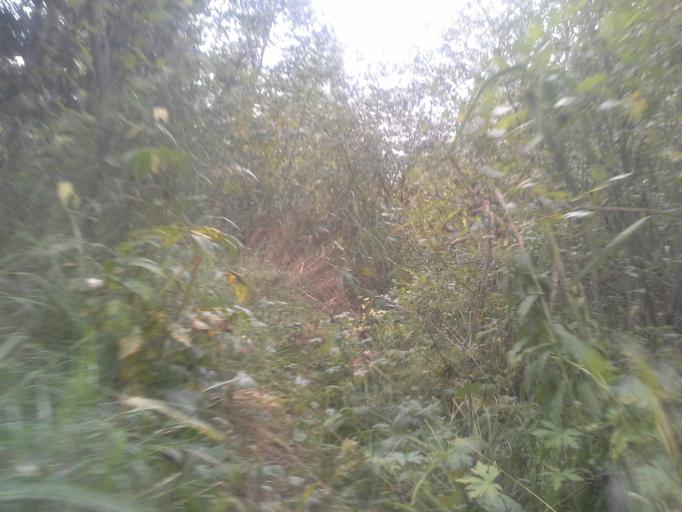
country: RU
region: Moskovskaya
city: Kievskij
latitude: 55.4260
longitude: 36.8821
